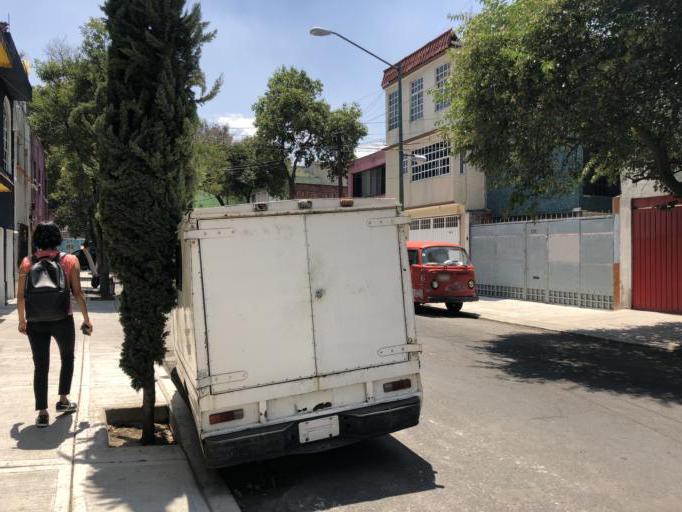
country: MX
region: Mexico City
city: Cuauhtemoc
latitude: 19.4571
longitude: -99.1368
